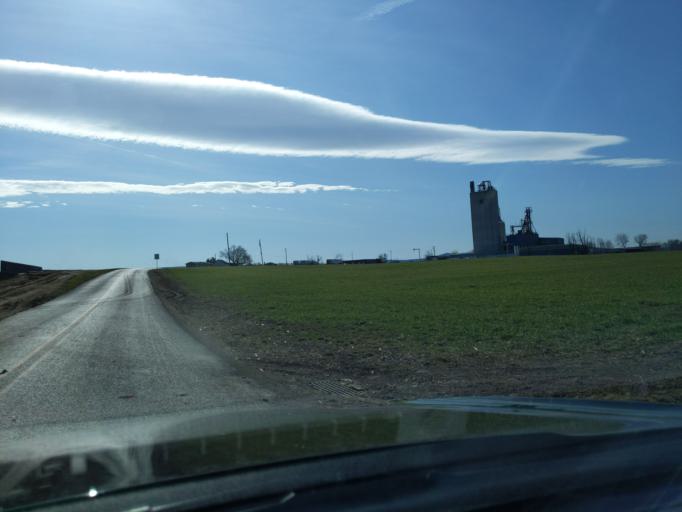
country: US
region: Pennsylvania
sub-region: Blair County
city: Martinsburg
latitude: 40.3157
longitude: -78.3469
